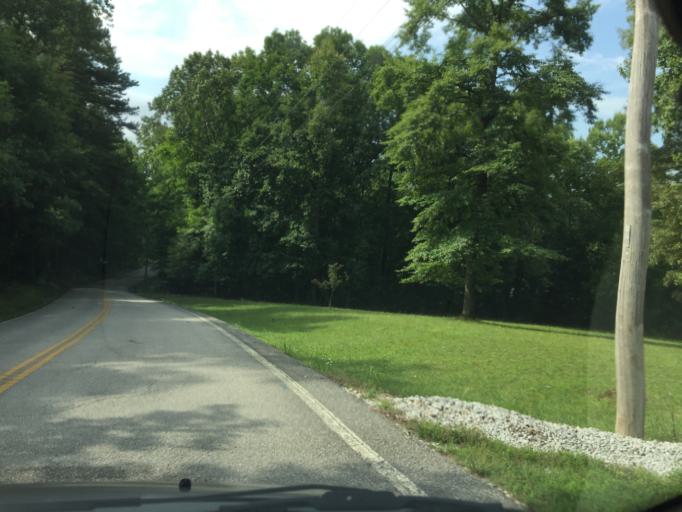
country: US
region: Tennessee
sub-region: Hamilton County
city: Apison
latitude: 35.0124
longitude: -85.0531
